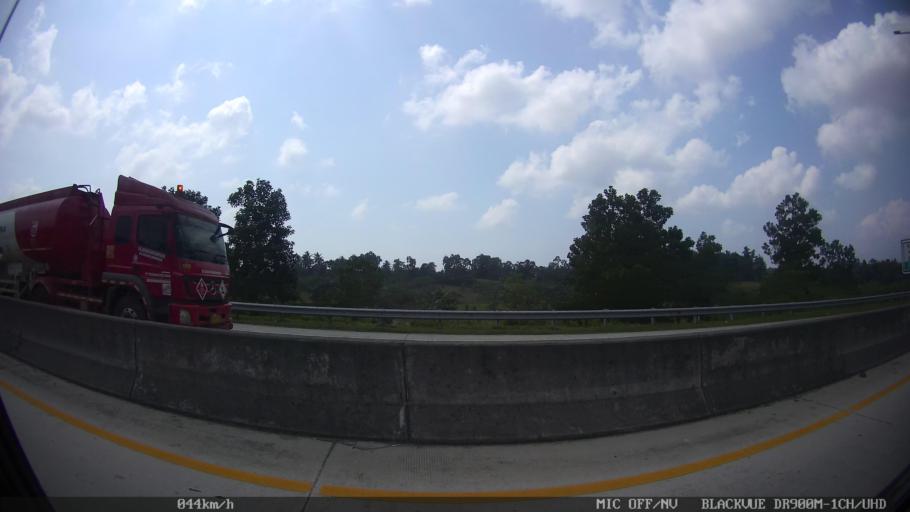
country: ID
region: Lampung
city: Natar
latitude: -5.2756
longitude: 105.2121
